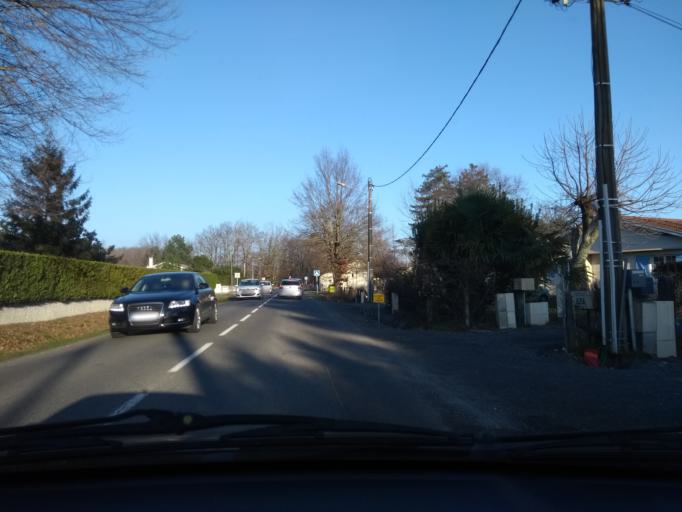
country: FR
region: Aquitaine
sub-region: Departement de la Gironde
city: Mios
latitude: 44.6096
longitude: -0.9288
